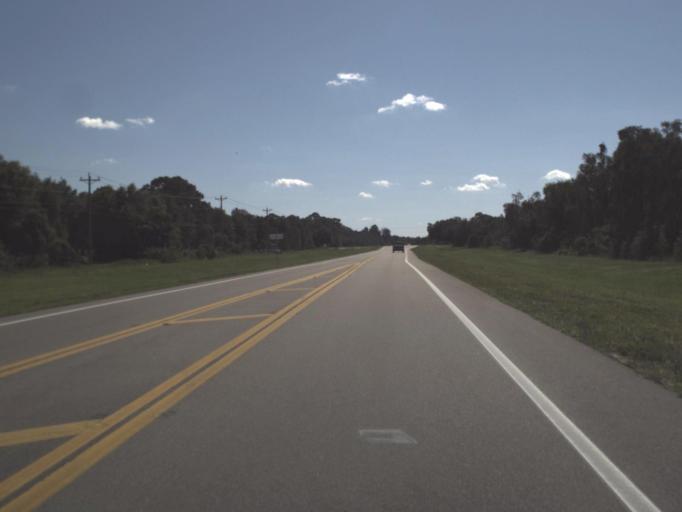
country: US
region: Florida
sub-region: Lee County
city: Lehigh Acres
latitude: 26.5591
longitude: -81.6615
